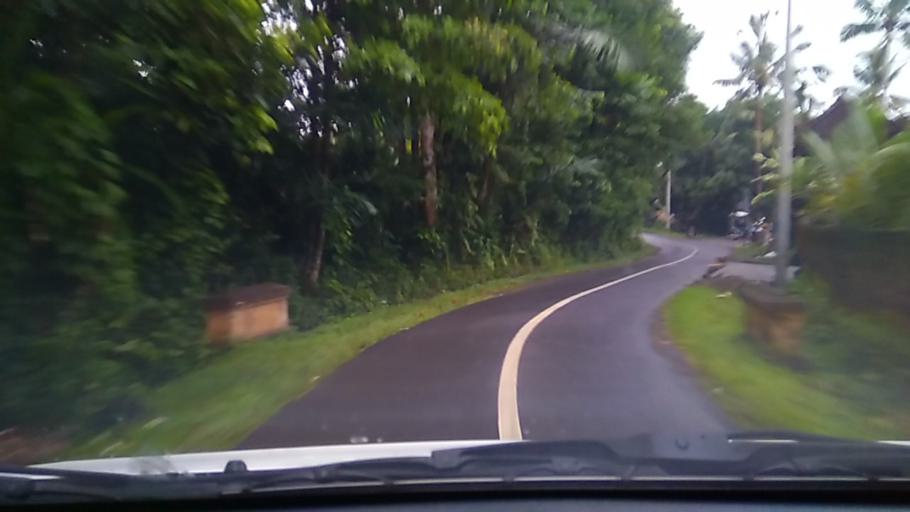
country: ID
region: Bali
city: Tiyingtali Kelod
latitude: -8.4083
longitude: 115.6216
